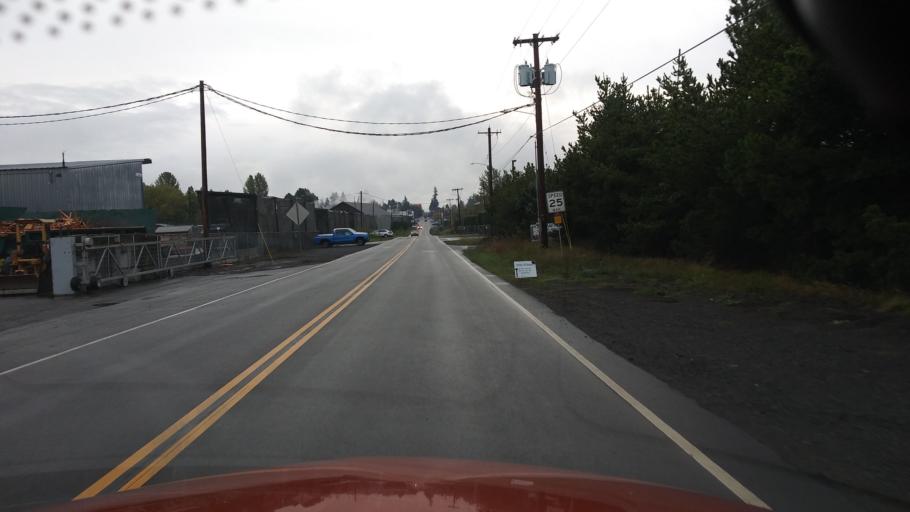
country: US
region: Oregon
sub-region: Washington County
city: North Plains
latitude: 45.5988
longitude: -123.0125
